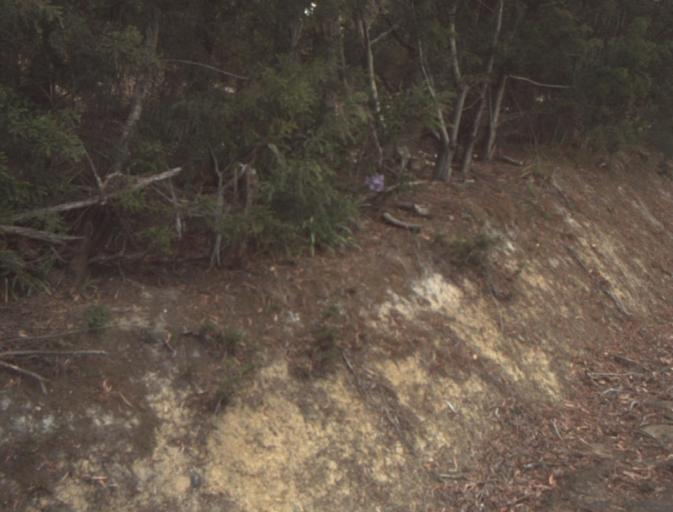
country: AU
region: Tasmania
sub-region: Launceston
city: Mayfield
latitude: -41.2164
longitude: 147.1702
